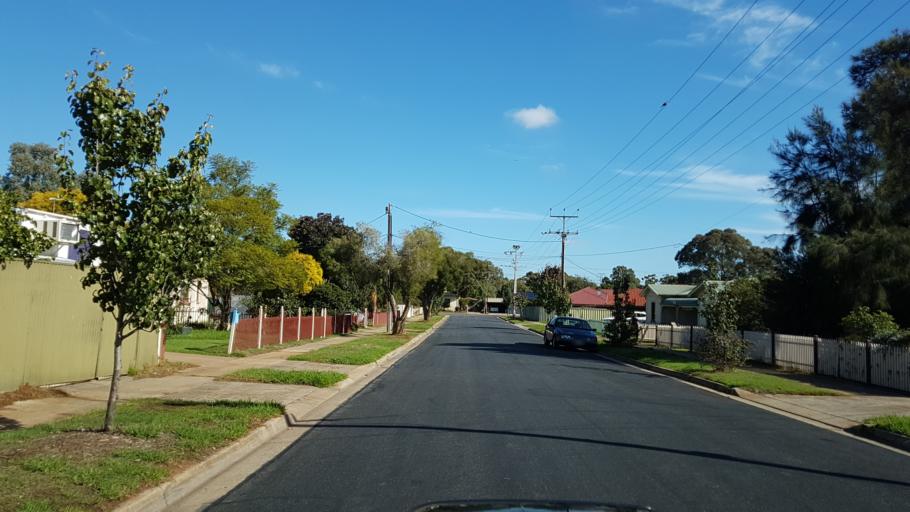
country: AU
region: South Australia
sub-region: Salisbury
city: Salisbury
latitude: -34.7542
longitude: 138.6394
